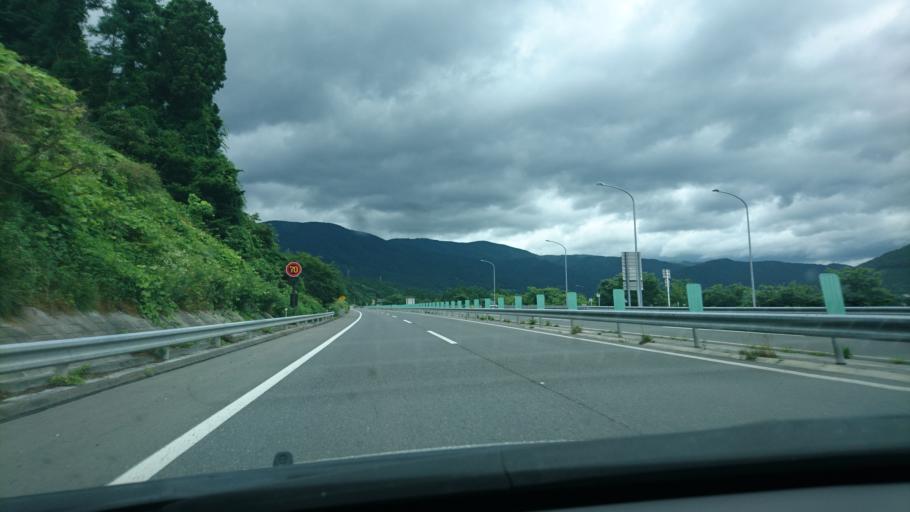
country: JP
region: Iwate
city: Ofunato
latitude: 39.1092
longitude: 141.7096
